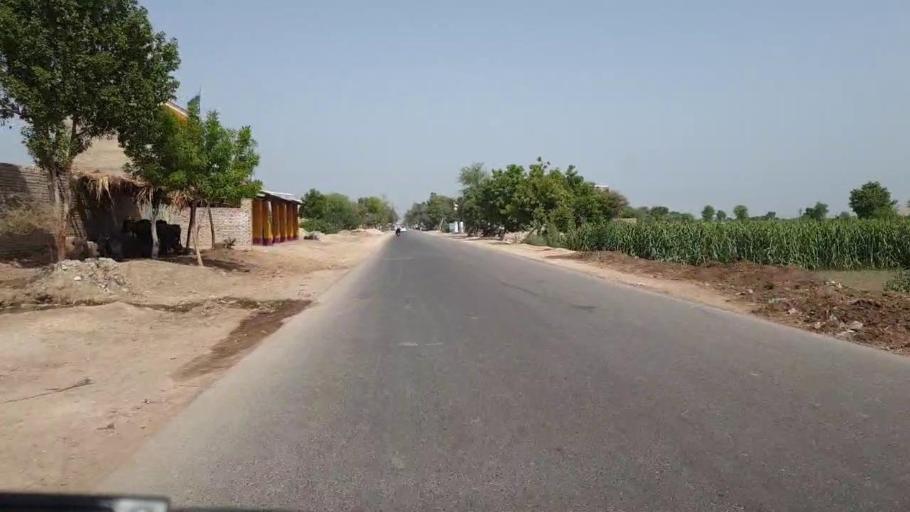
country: PK
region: Sindh
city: Sakrand
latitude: 26.2754
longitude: 68.1514
